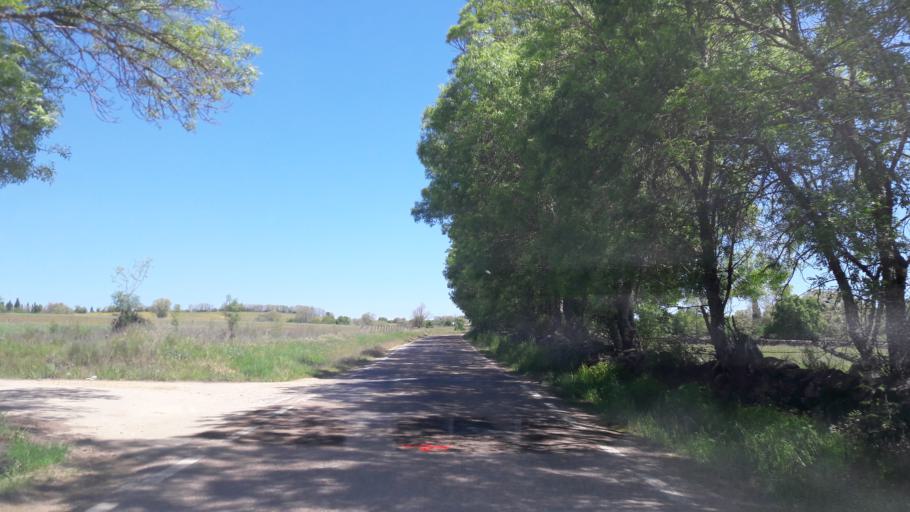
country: ES
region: Castille and Leon
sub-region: Provincia de Salamanca
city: Endrinal
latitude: 40.5660
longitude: -5.8089
